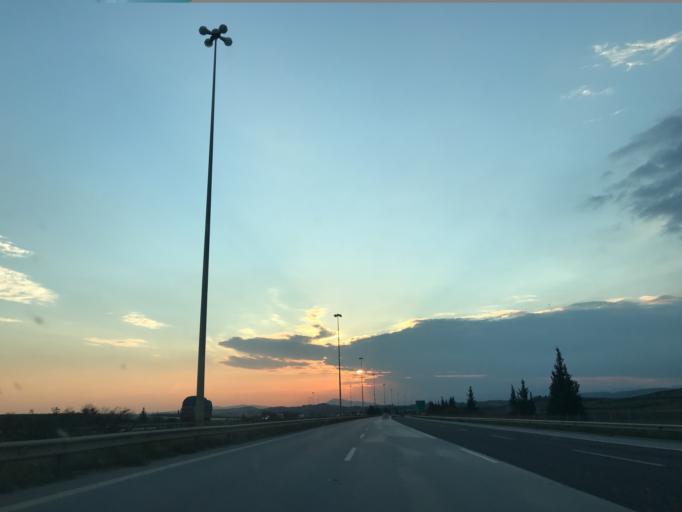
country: TR
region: Mersin
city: Yenice
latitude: 37.0098
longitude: 34.9825
